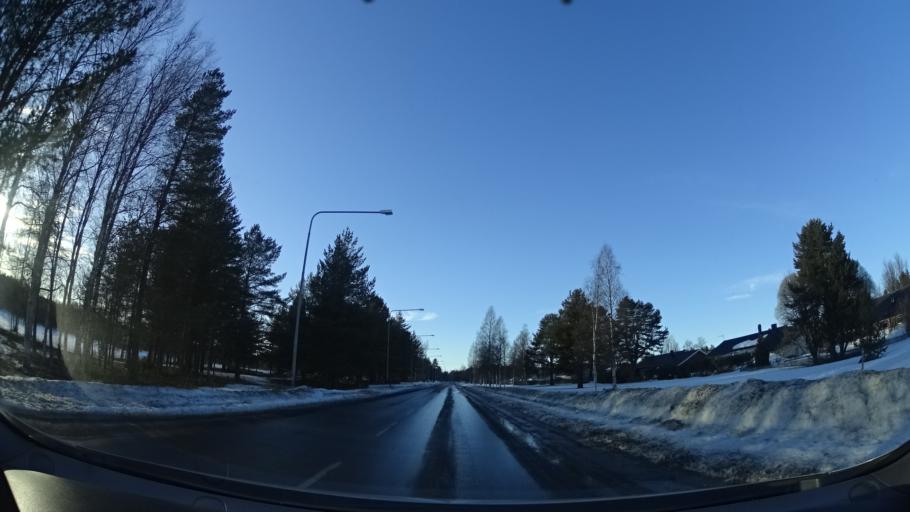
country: SE
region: Vaesterbotten
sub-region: Skelleftea Kommun
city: Byske
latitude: 64.9469
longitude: 21.2279
